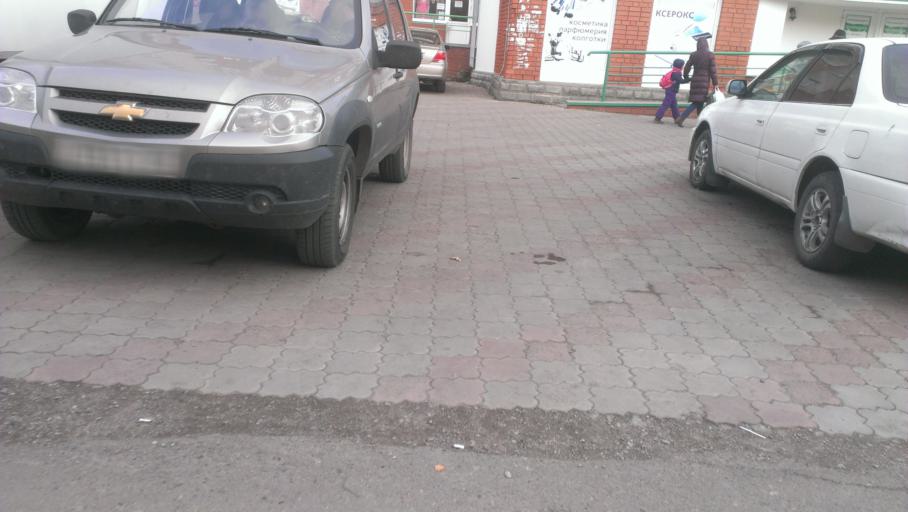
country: RU
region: Altai Krai
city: Novosilikatnyy
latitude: 53.3412
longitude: 83.6709
